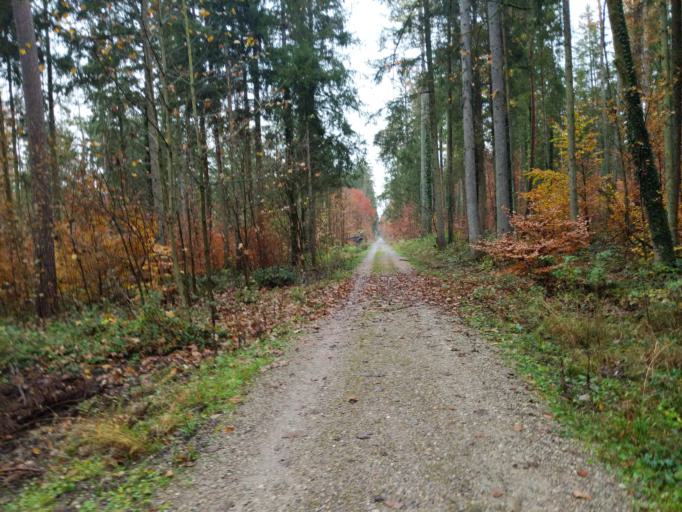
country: DE
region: Bavaria
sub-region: Upper Bavaria
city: Zorneding
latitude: 48.0918
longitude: 11.8490
